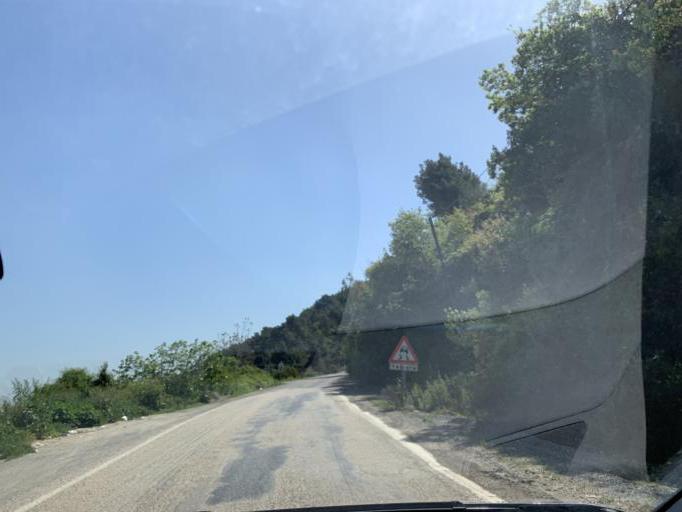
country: TR
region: Bursa
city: Niluefer
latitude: 40.3553
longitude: 28.9777
